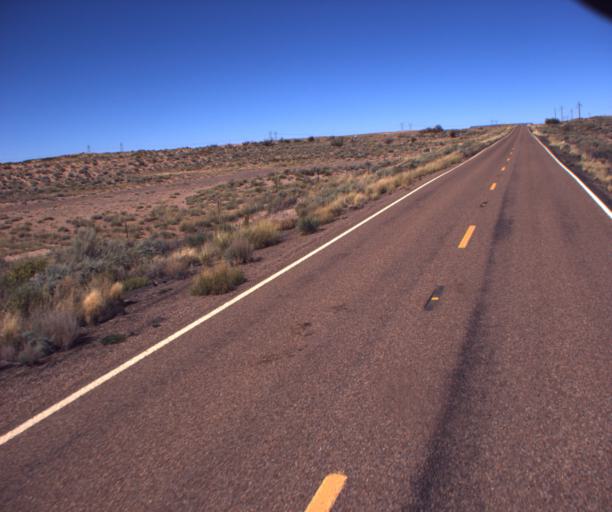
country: US
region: Arizona
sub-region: Navajo County
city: Holbrook
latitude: 35.1357
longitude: -110.0904
